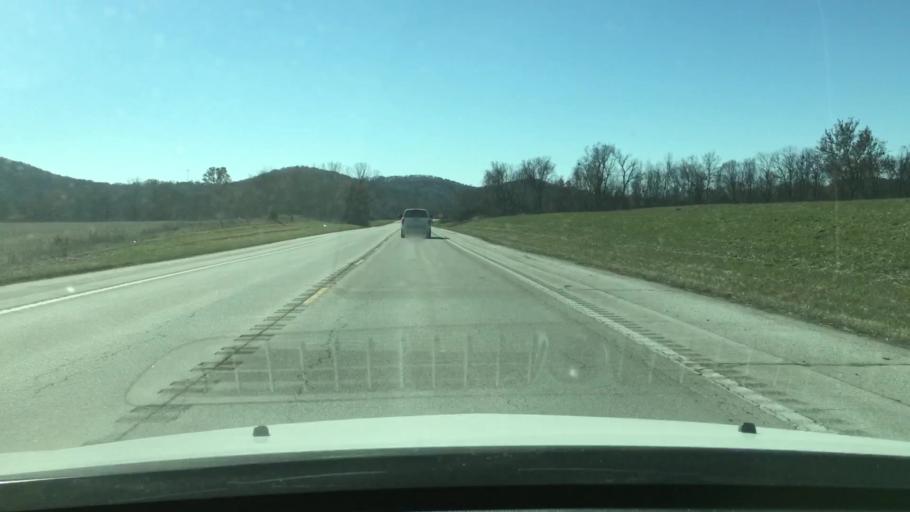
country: US
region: Missouri
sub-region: Pike County
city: Louisiana
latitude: 39.4256
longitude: -91.0846
